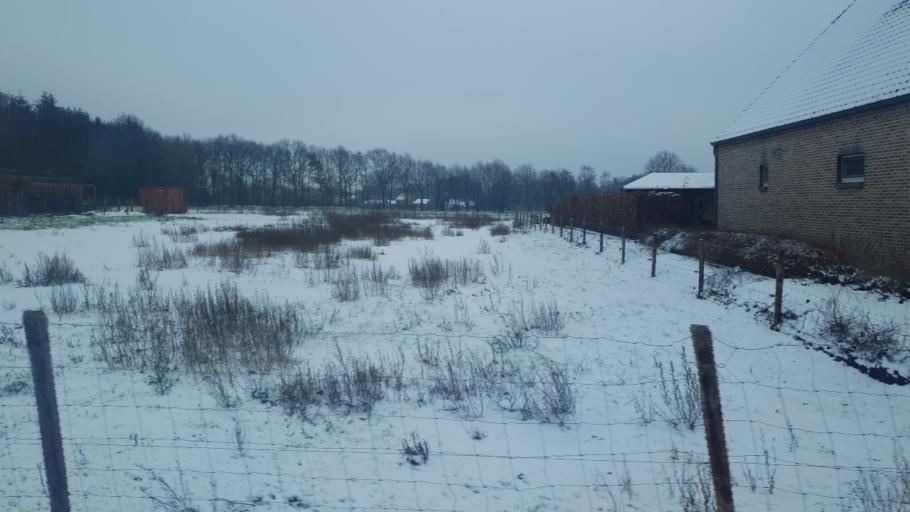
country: BE
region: Flanders
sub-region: Provincie Limburg
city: Overpelt
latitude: 51.1992
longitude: 5.4295
